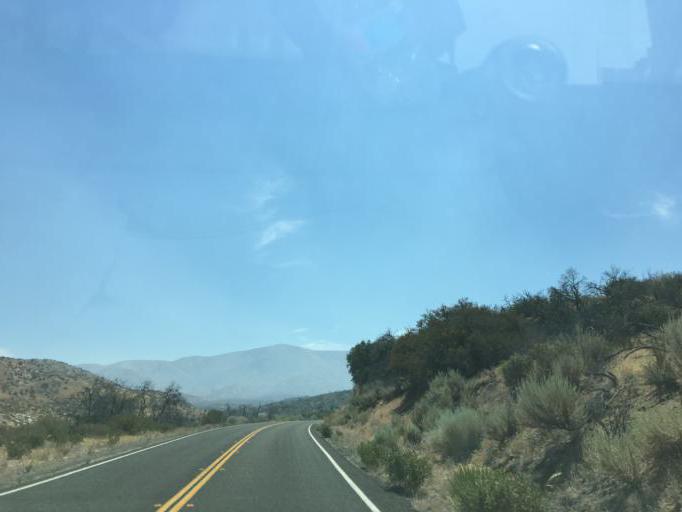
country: US
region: California
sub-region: Los Angeles County
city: Vincent
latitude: 34.4299
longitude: -118.1207
